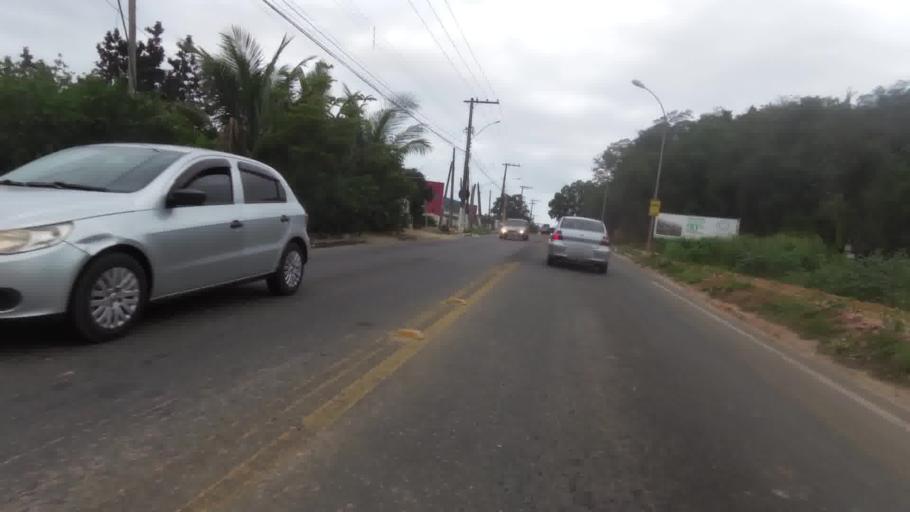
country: BR
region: Espirito Santo
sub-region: Piuma
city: Piuma
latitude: -20.8073
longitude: -40.6635
